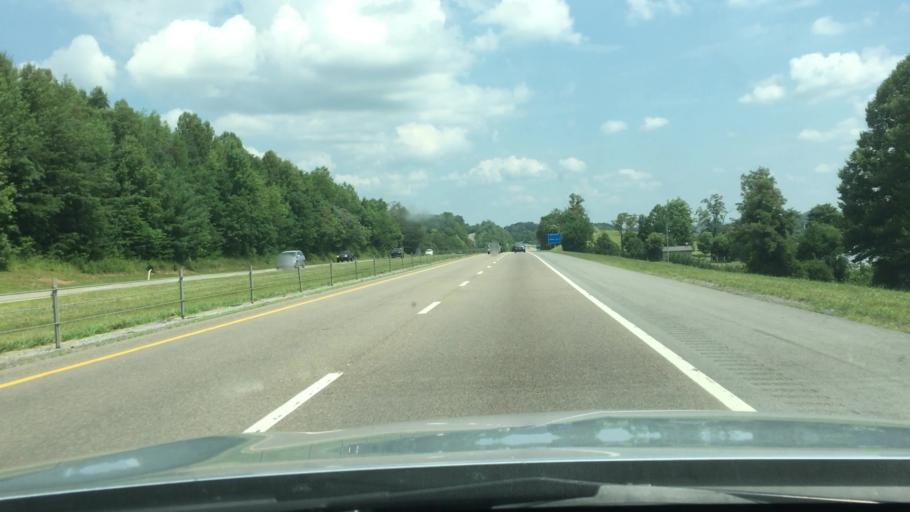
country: US
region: Tennessee
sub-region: Carter County
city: Pine Crest
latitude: 36.2454
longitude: -82.3259
